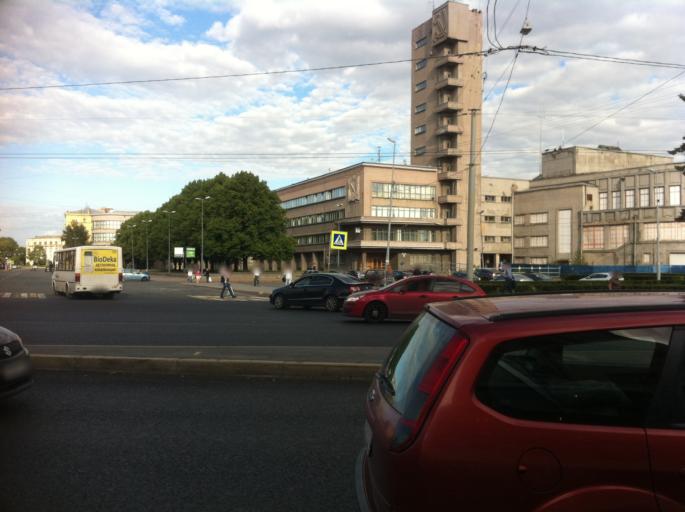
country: RU
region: St.-Petersburg
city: Admiralteisky
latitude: 59.8949
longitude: 30.2753
